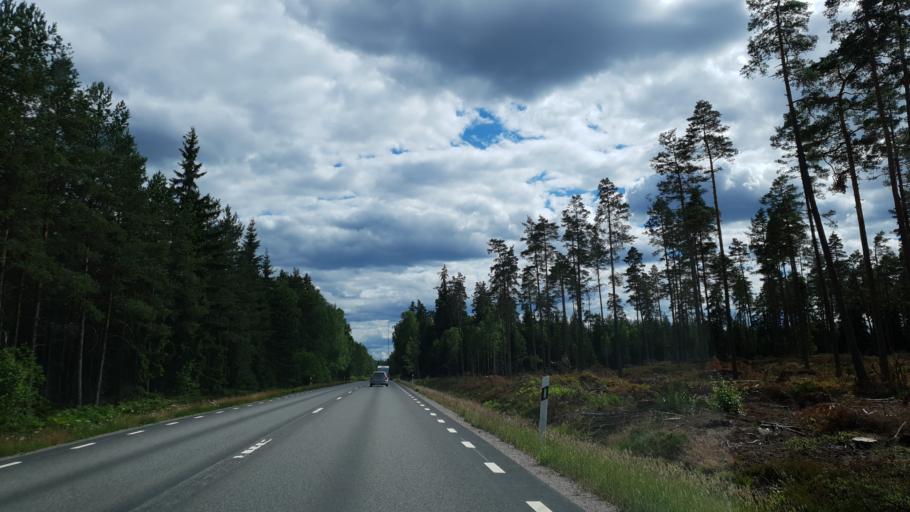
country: SE
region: Kronoberg
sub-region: Lessebo Kommun
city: Lessebo
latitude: 56.7881
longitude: 15.4141
